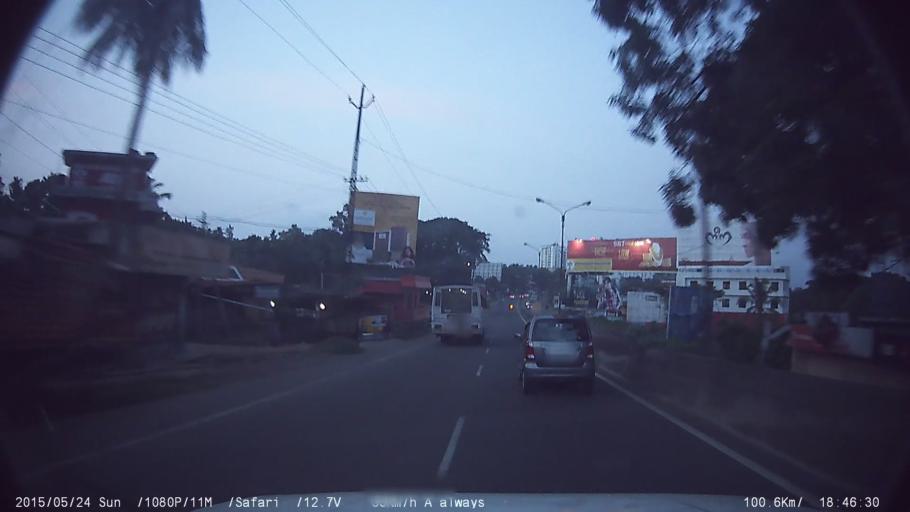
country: IN
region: Kerala
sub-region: Ernakulam
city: Aluva
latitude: 10.1279
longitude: 76.3427
